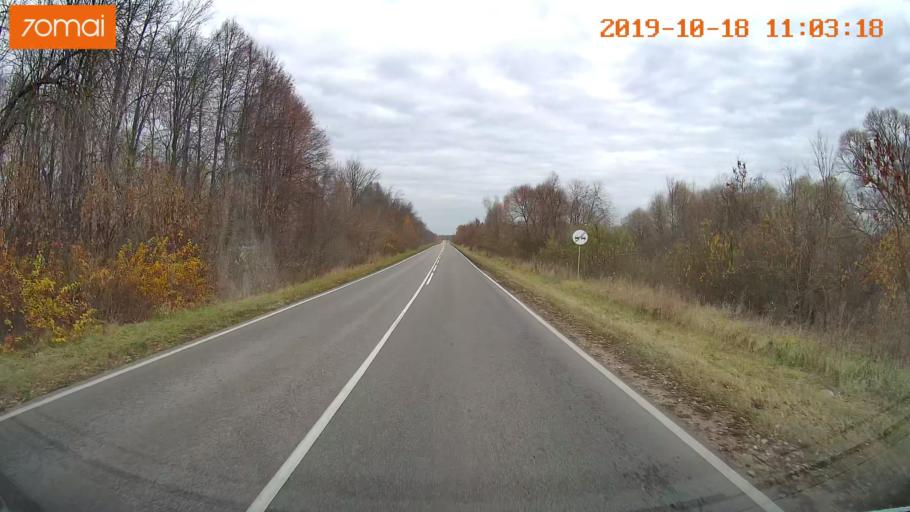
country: RU
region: Tula
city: Yepifan'
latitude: 53.8776
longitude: 38.5482
